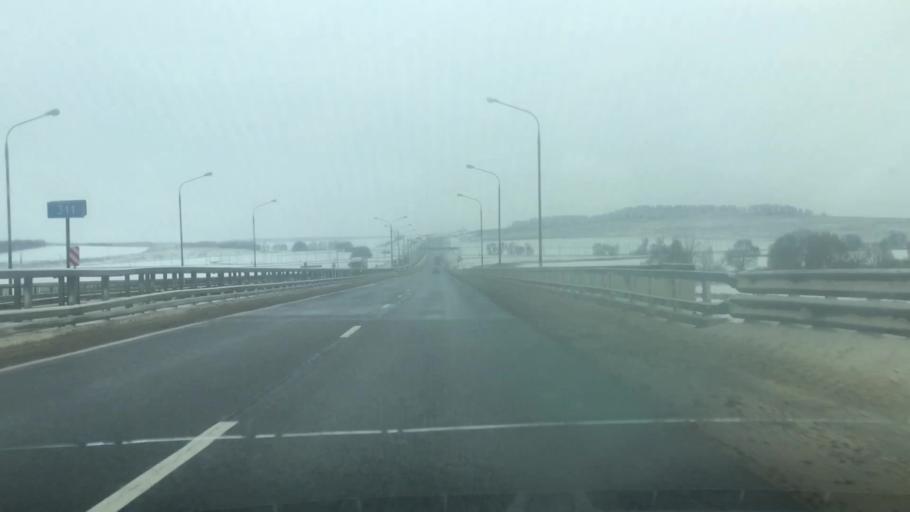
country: RU
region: Tula
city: Yefremov
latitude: 53.1707
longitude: 38.2461
